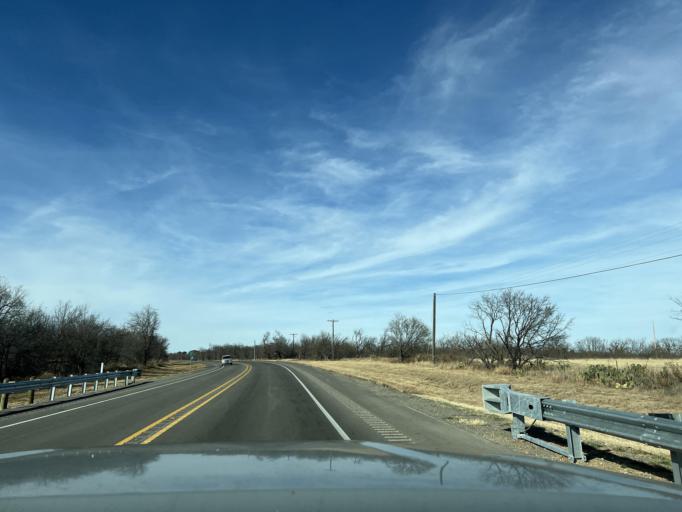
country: US
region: Texas
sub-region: Shackelford County
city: Albany
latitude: 32.5718
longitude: -99.1766
